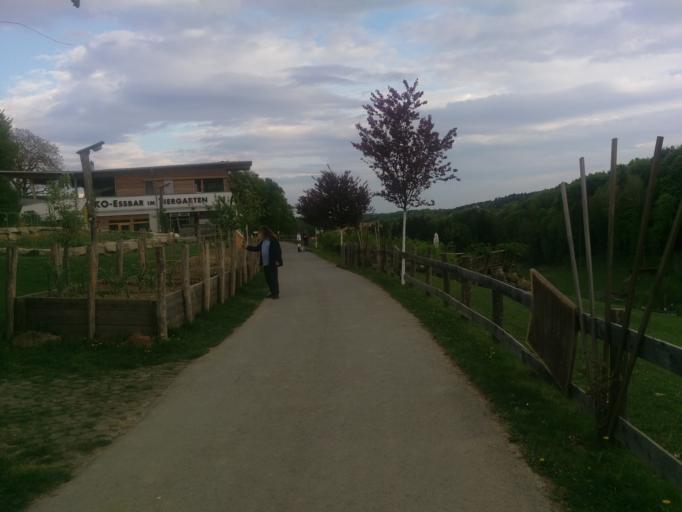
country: AT
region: Styria
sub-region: Politischer Bezirk Suedoststeiermark
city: Riegersburg
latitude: 46.9907
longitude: 15.9109
